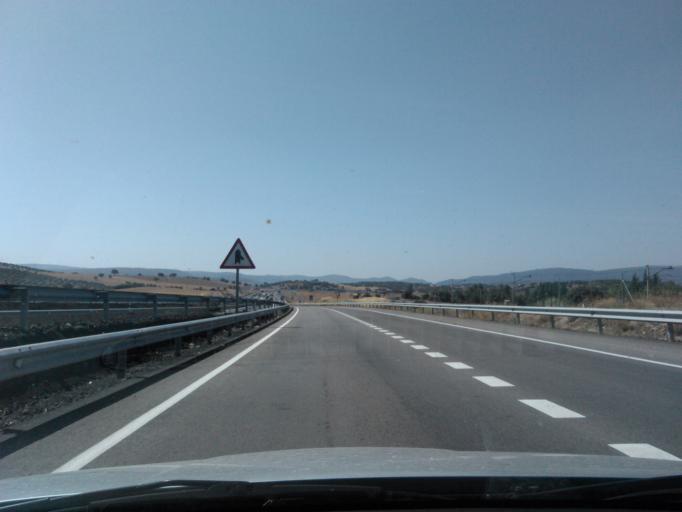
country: ES
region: Castille-La Mancha
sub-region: Provincia de Ciudad Real
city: Viso del Marques
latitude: 38.4951
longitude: -3.5049
